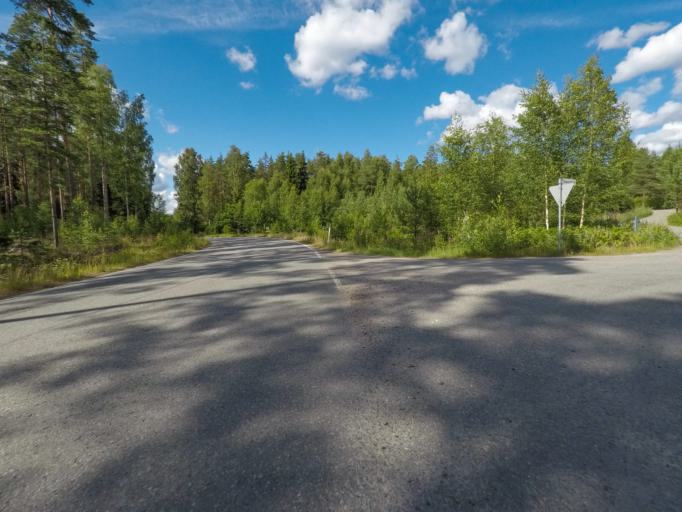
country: FI
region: South Karelia
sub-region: Lappeenranta
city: Joutseno
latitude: 61.1070
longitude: 28.3726
